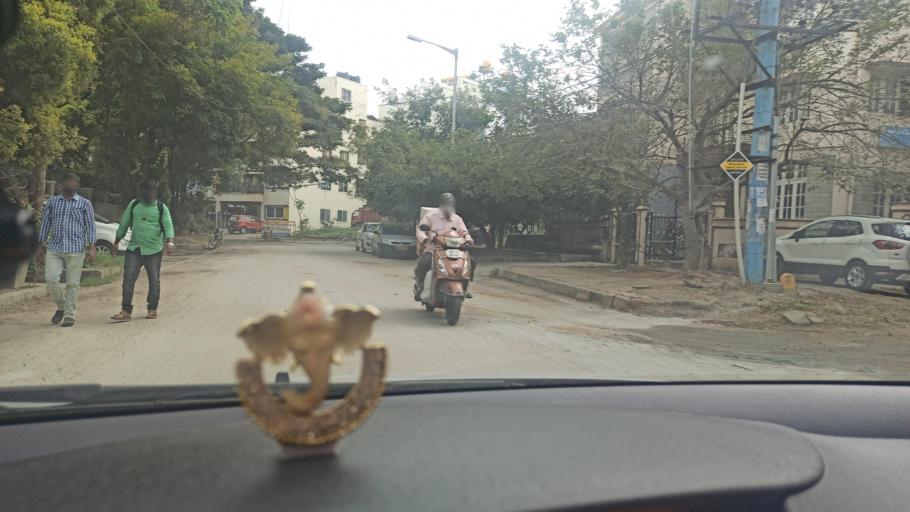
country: IN
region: Karnataka
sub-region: Bangalore Urban
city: Bangalore
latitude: 12.9146
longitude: 77.6266
